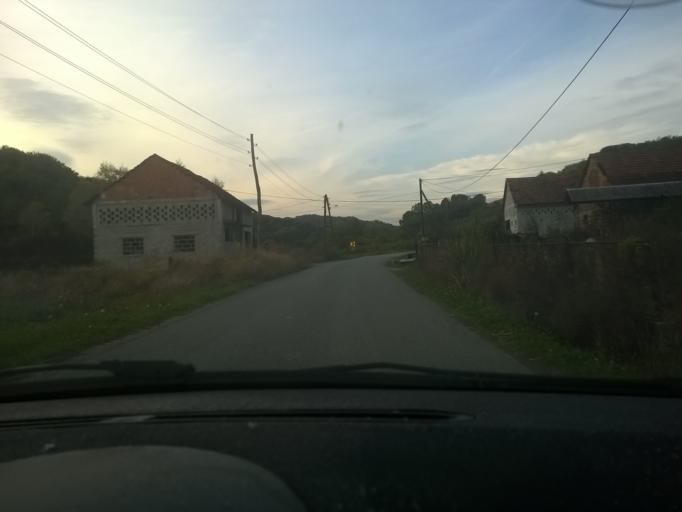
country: HR
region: Krapinsko-Zagorska
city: Zabok
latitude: 46.0839
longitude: 15.8916
